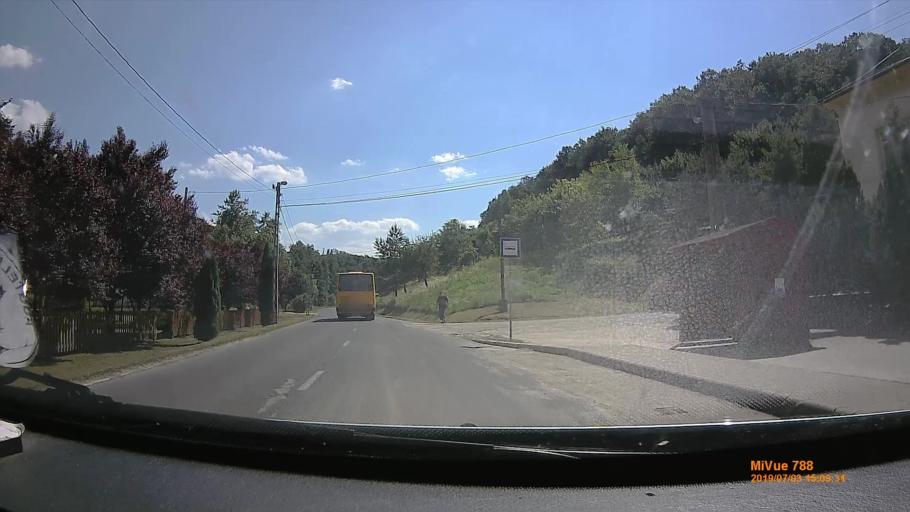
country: HU
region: Borsod-Abauj-Zemplen
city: Ozd
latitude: 48.2369
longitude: 20.3729
